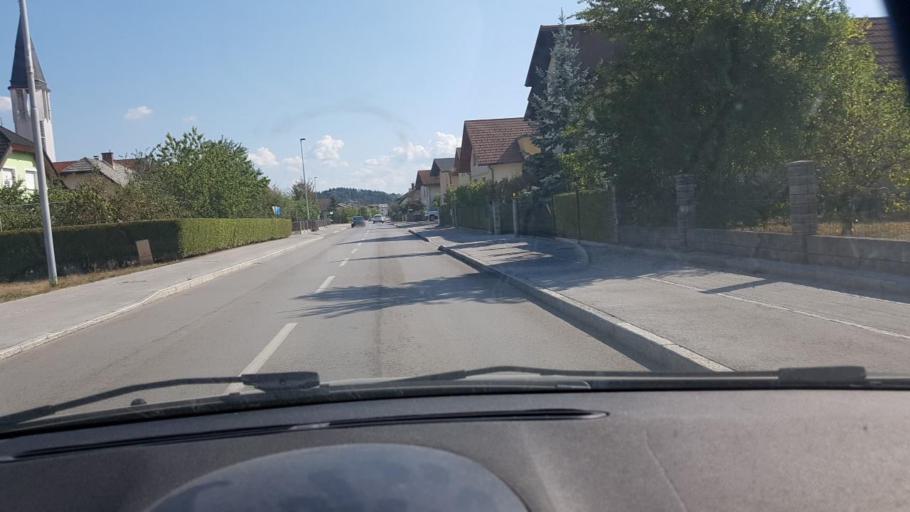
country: SI
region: Domzale
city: Vir
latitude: 46.1573
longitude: 14.6052
